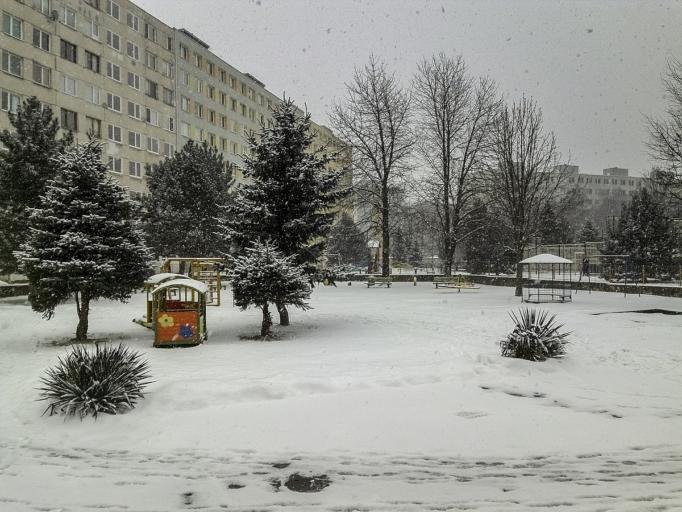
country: SK
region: Kosicky
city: Kosice
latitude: 48.7082
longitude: 21.2437
